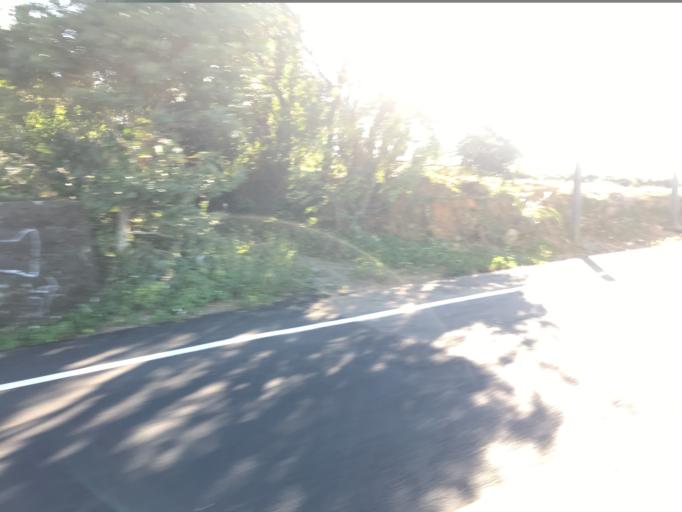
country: TW
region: Taiwan
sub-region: Hsinchu
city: Zhubei
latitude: 24.8686
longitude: 121.0920
